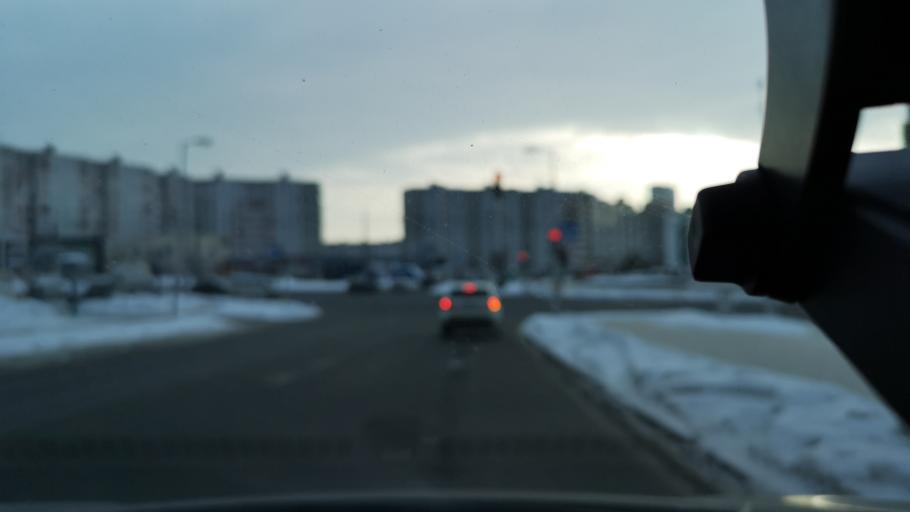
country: BY
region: Minsk
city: Borovlyany
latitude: 53.9530
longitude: 27.6810
